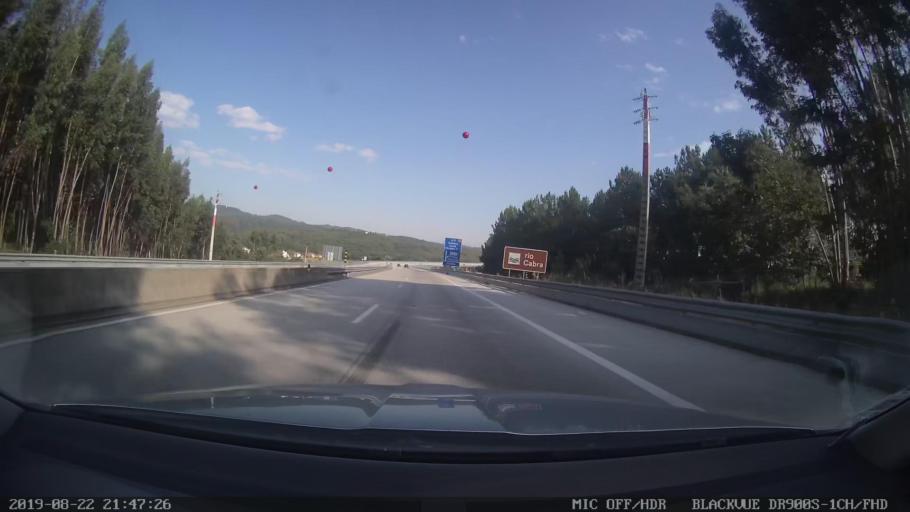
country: PT
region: Coimbra
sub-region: Penela
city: Penela
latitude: 40.0059
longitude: -8.3645
